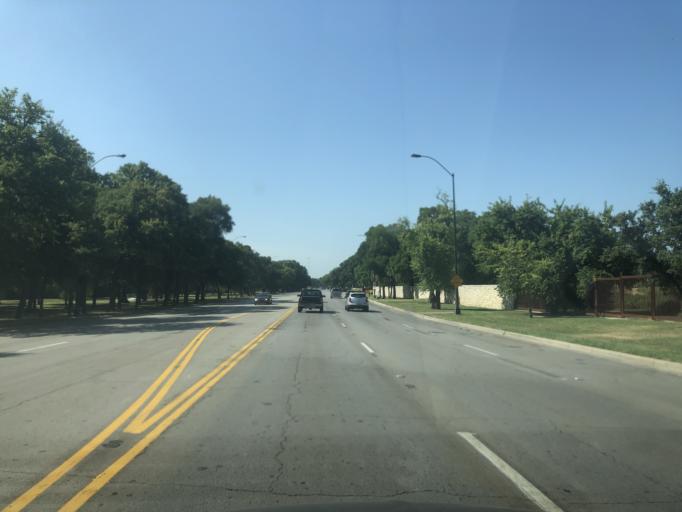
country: US
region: Texas
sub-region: Tarrant County
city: Fort Worth
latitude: 32.7424
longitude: -97.3615
